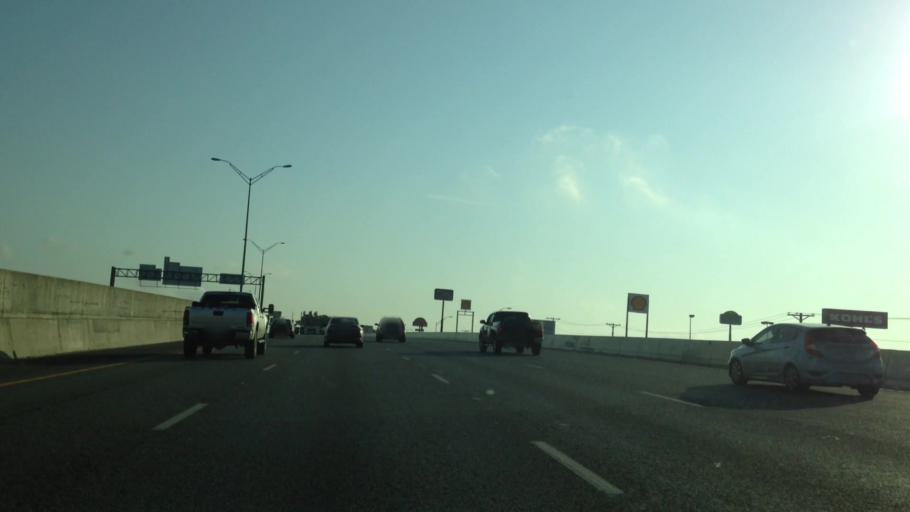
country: US
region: Texas
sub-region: Comal County
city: New Braunfels
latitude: 29.6979
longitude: -98.0949
